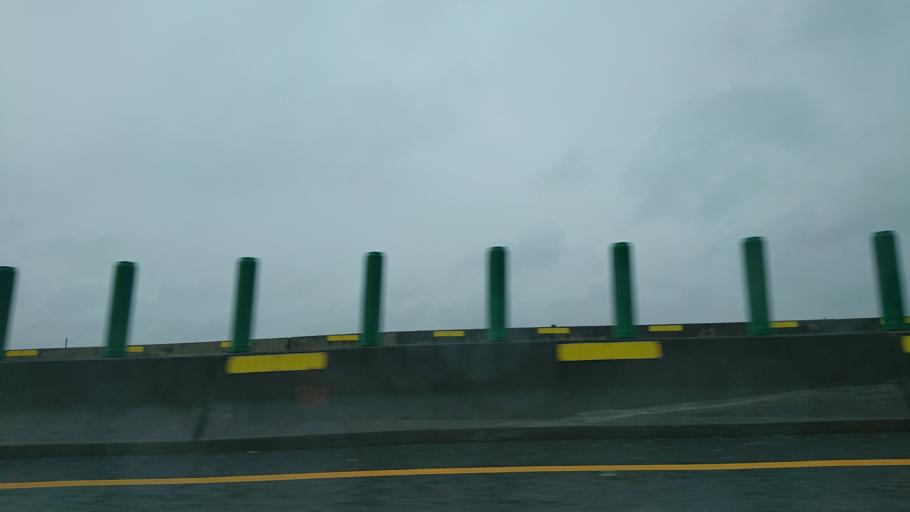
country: TW
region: Taiwan
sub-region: Chiayi
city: Taibao
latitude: 23.7193
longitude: 120.2148
